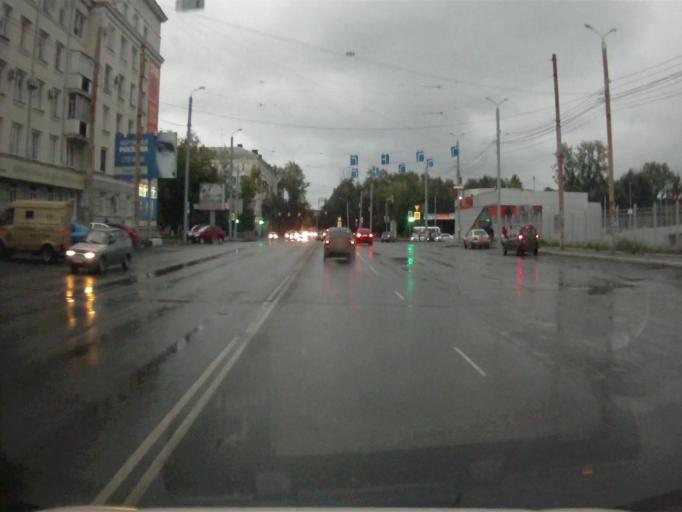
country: RU
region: Chelyabinsk
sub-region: Gorod Chelyabinsk
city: Chelyabinsk
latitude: 55.1623
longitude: 61.4339
